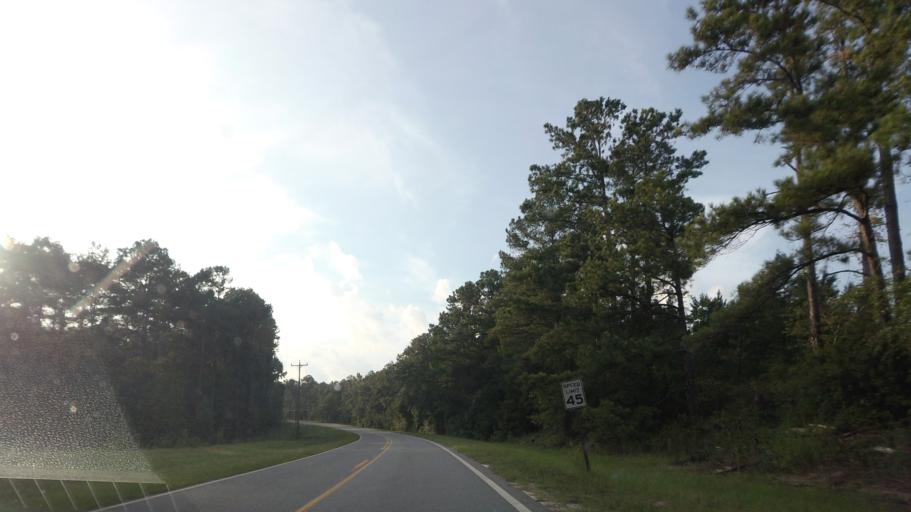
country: US
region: Georgia
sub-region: Wilkinson County
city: Gordon
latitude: 32.8226
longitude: -83.4060
